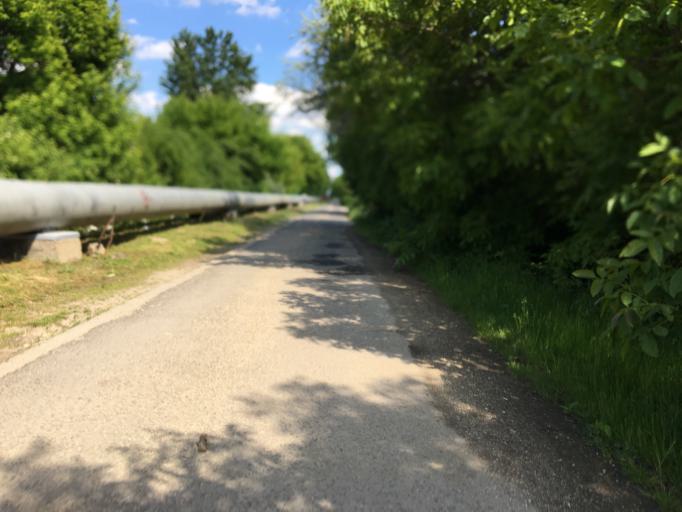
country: HU
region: Budapest
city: Budapest III. keruelet
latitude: 47.5696
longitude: 19.0386
